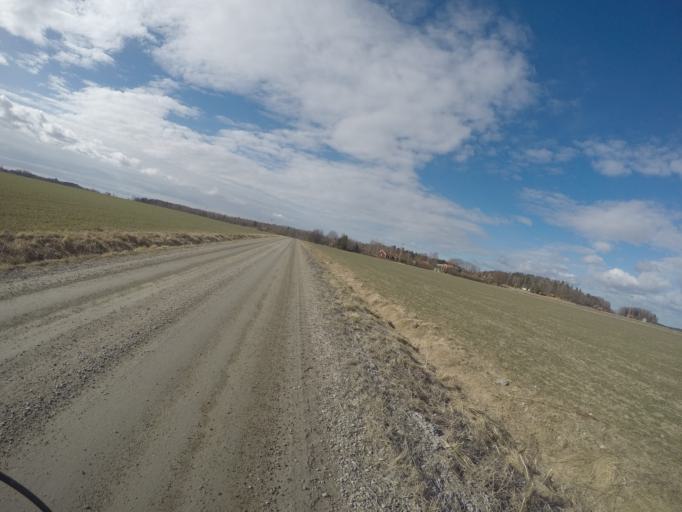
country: SE
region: Soedermanland
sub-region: Eskilstuna Kommun
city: Kvicksund
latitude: 59.4116
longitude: 16.2631
